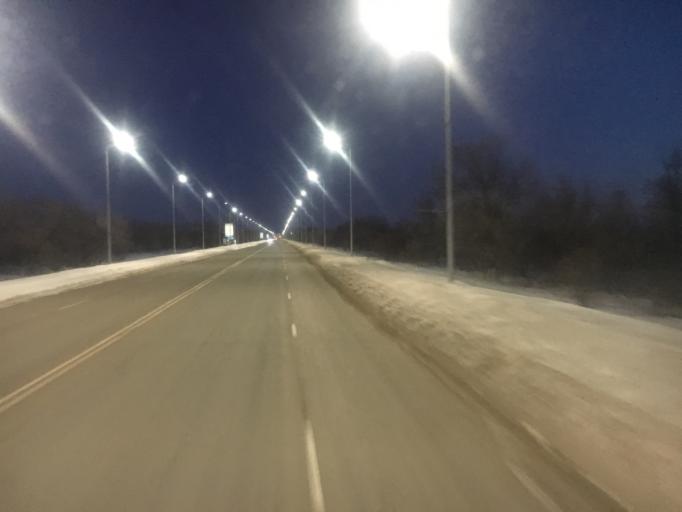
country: KZ
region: Batys Qazaqstan
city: Oral
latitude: 51.1620
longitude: 51.5280
